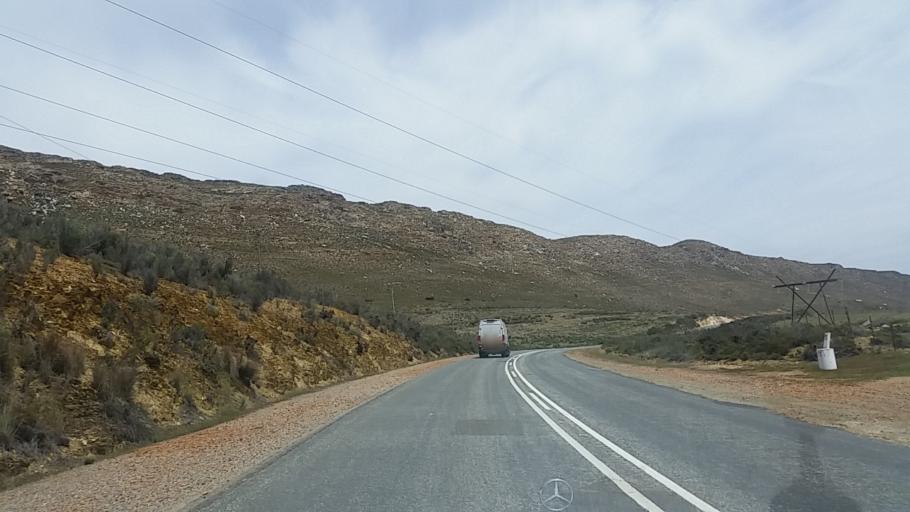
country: ZA
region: Western Cape
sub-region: Eden District Municipality
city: Knysna
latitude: -33.7396
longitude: 23.0384
